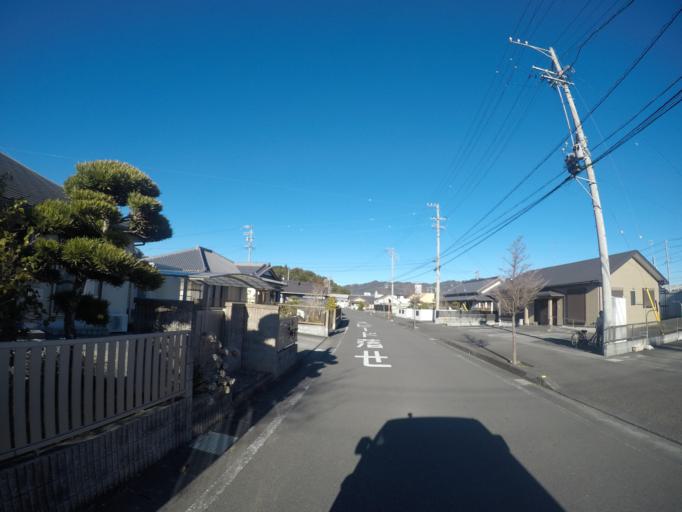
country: JP
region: Shizuoka
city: Fujieda
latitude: 34.8794
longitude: 138.2711
